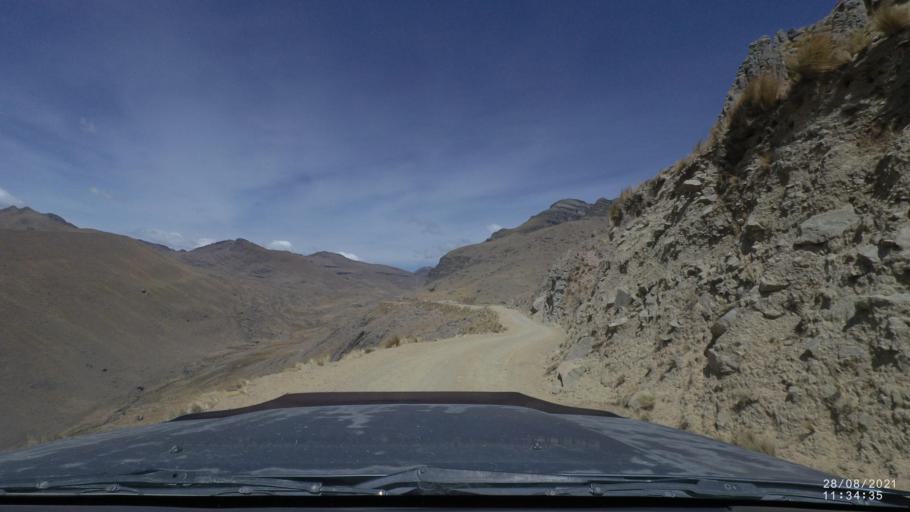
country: BO
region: Cochabamba
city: Sipe Sipe
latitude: -17.1918
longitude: -66.3742
